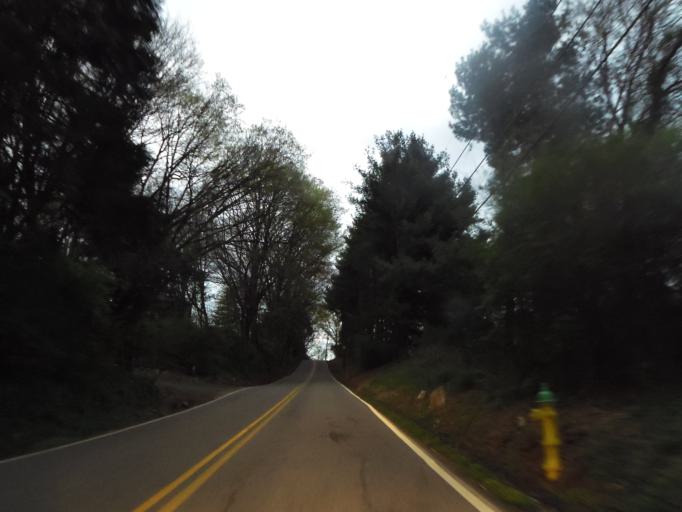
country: US
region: Tennessee
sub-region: Knox County
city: Farragut
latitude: 35.9320
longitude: -84.0587
